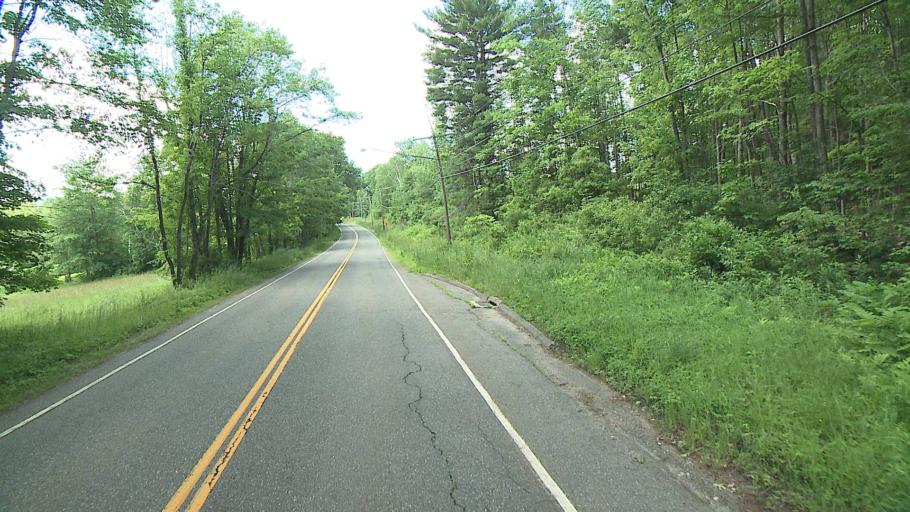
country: US
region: Connecticut
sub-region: Litchfield County
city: West Torrington
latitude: 41.8383
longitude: -73.1585
